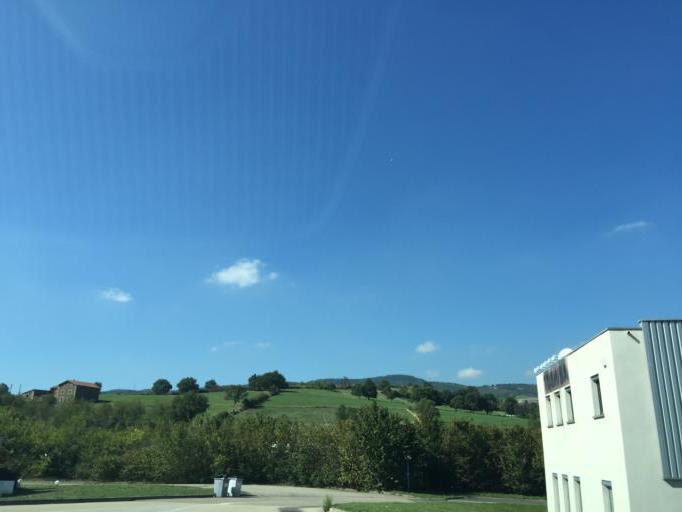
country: FR
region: Rhone-Alpes
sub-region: Departement de la Loire
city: Saint-Chamond
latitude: 45.4921
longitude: 4.5251
